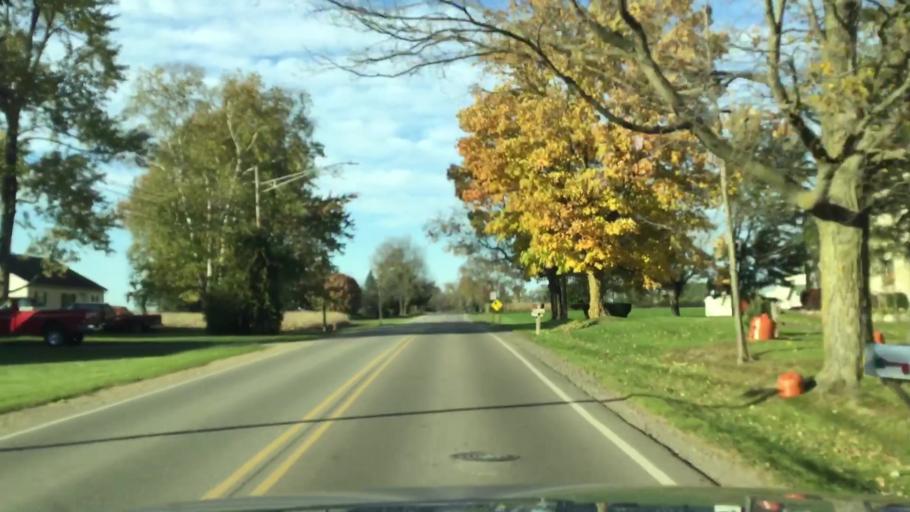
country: US
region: Michigan
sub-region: Lapeer County
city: North Branch
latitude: 43.2341
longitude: -83.1960
